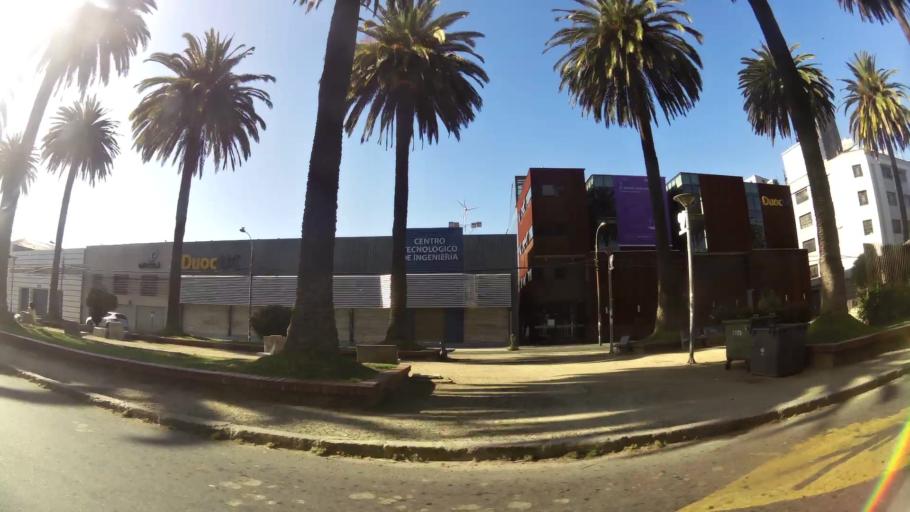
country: CL
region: Valparaiso
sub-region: Provincia de Valparaiso
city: Valparaiso
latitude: -33.0448
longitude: -71.6155
